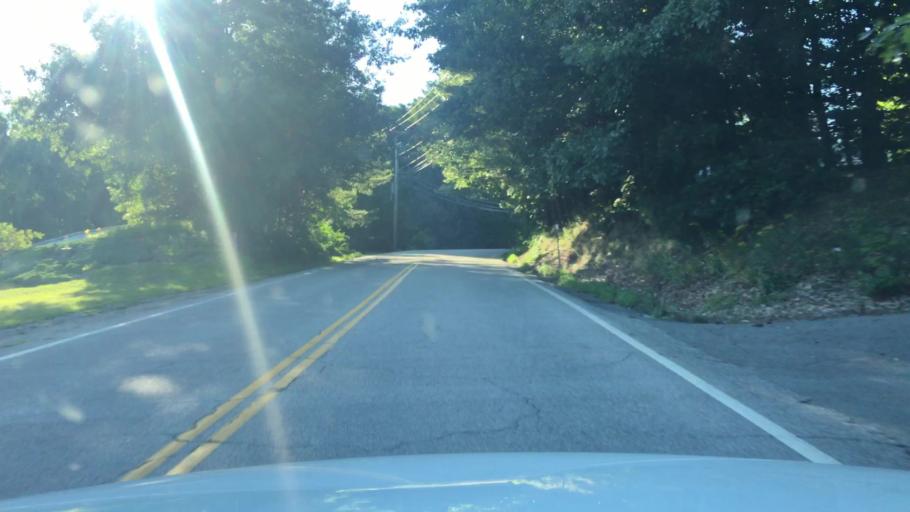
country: US
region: New Hampshire
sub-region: Rockingham County
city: Sandown
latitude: 42.9168
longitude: -71.1664
